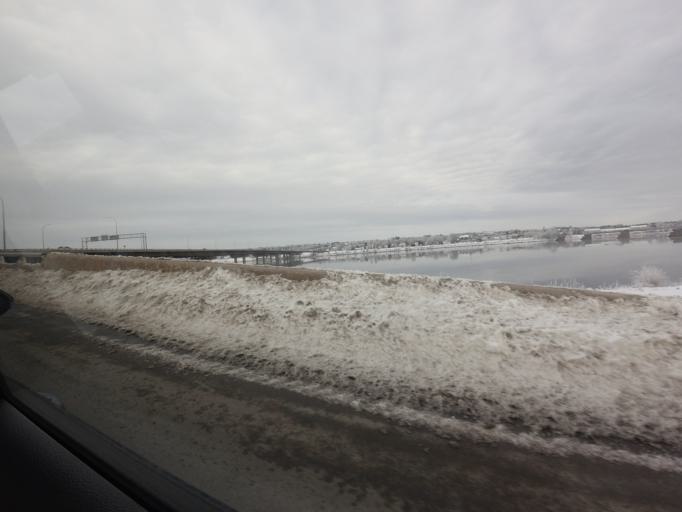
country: CA
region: New Brunswick
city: Fredericton
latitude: 45.9653
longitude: -66.6430
